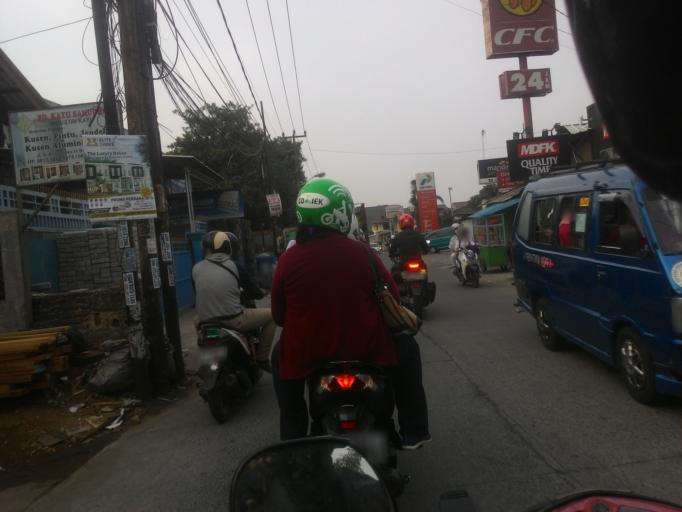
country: ID
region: West Java
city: Depok
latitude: -6.3746
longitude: 106.8131
